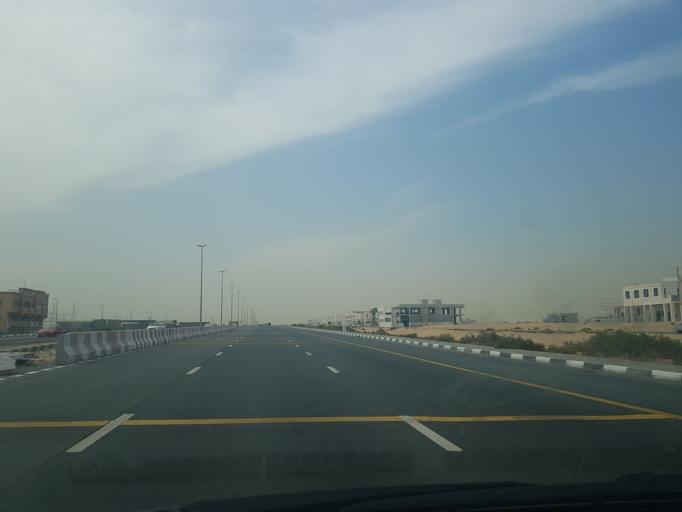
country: AE
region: Ash Shariqah
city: Sharjah
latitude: 25.2493
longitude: 55.5376
